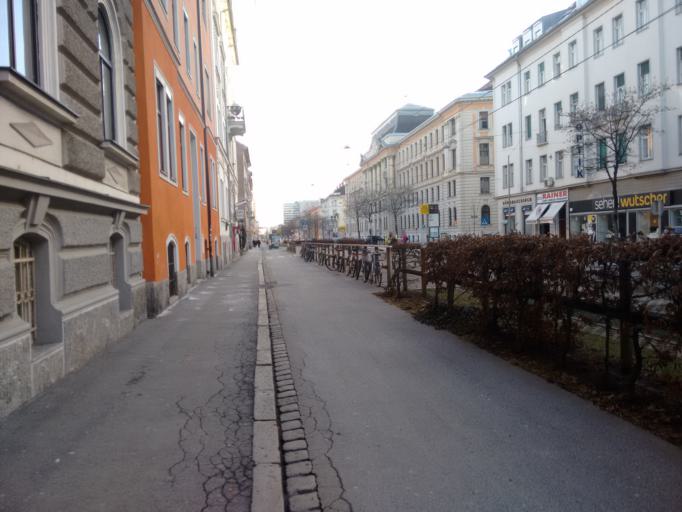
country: AT
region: Styria
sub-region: Graz Stadt
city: Graz
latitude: 47.0636
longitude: 15.4432
